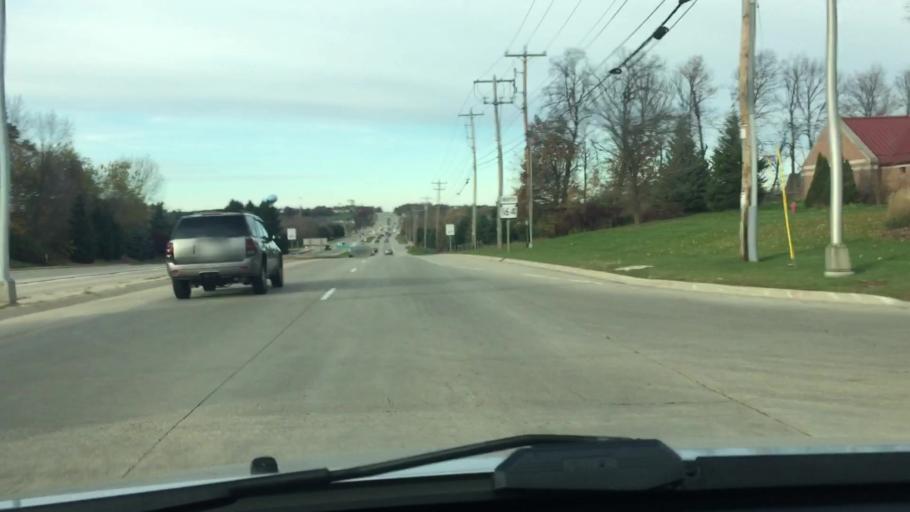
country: US
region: Wisconsin
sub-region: Waukesha County
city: Pewaukee
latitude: 43.0606
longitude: -88.2251
